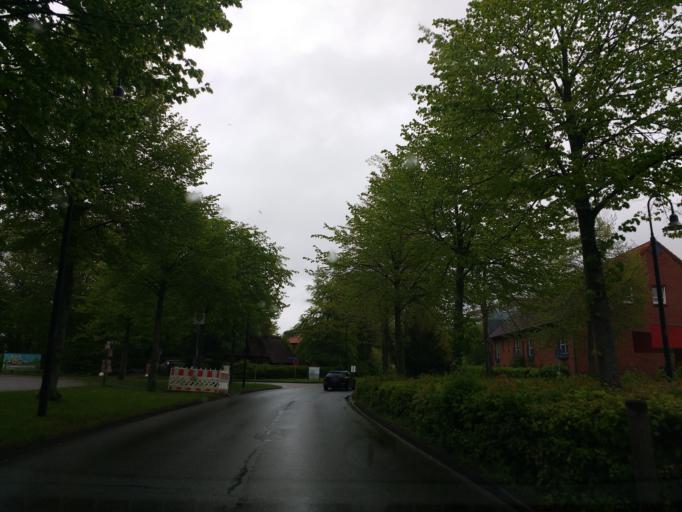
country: DE
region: Schleswig-Holstein
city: Damp
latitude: 54.5810
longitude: 10.0174
